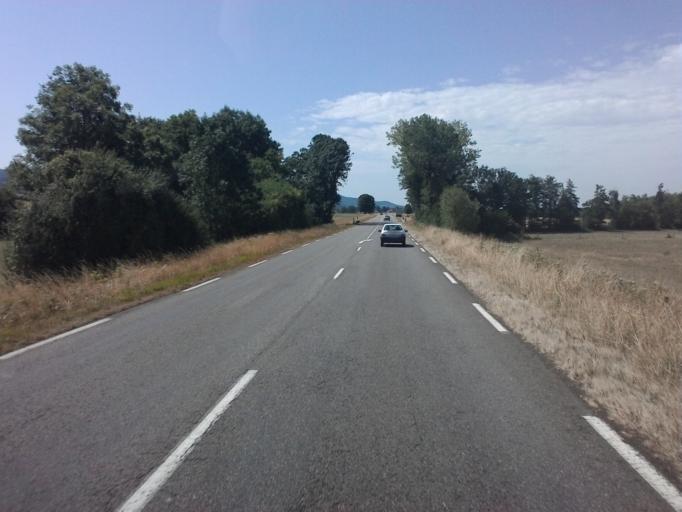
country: FR
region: Franche-Comte
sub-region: Departement du Jura
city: Montmorot
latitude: 46.6212
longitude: 5.4845
